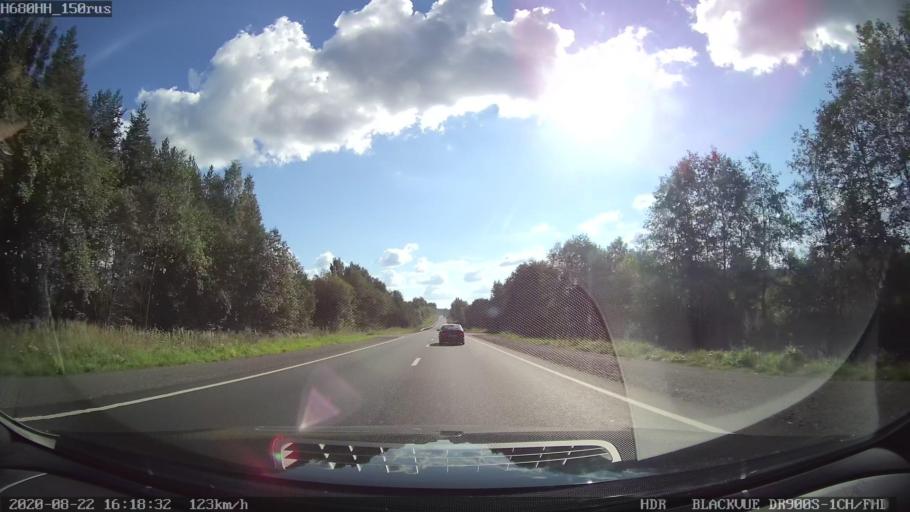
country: RU
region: Tverskaya
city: Rameshki
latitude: 57.4152
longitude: 36.1384
